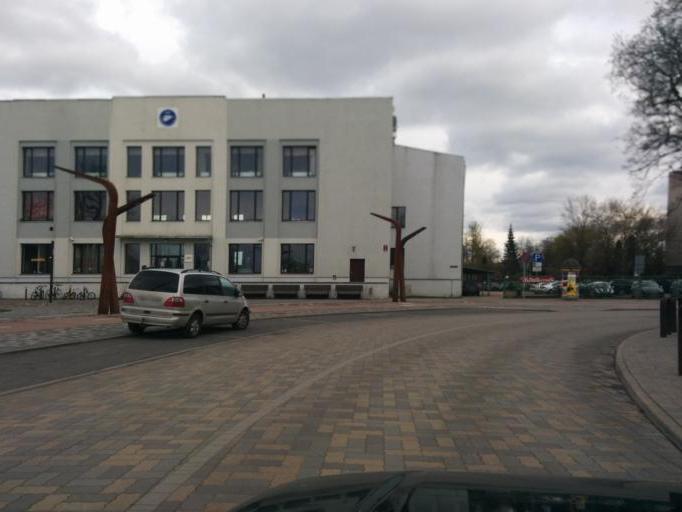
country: LV
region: Jelgava
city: Jelgava
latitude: 56.6500
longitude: 23.7327
